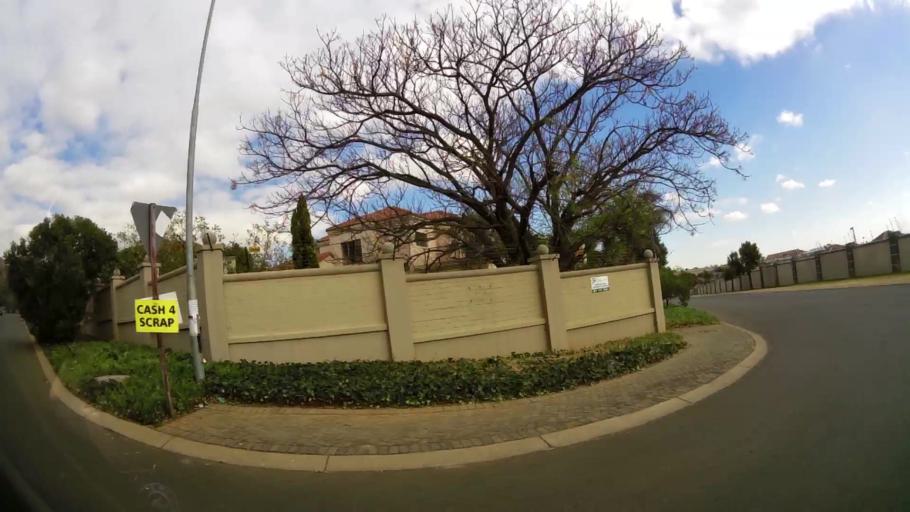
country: ZA
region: Gauteng
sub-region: City of Johannesburg Metropolitan Municipality
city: Roodepoort
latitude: -26.0970
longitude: 27.8720
